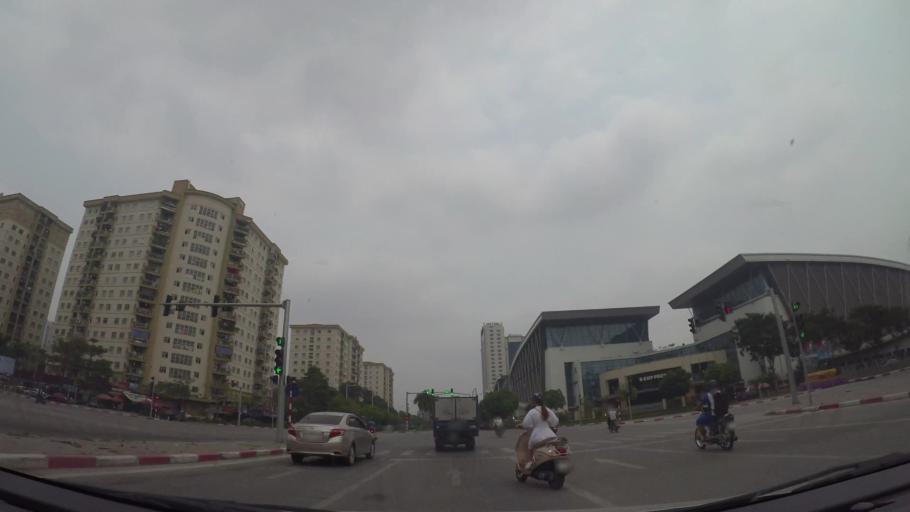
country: VN
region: Ha Noi
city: Cau Dien
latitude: 21.0292
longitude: 105.7638
